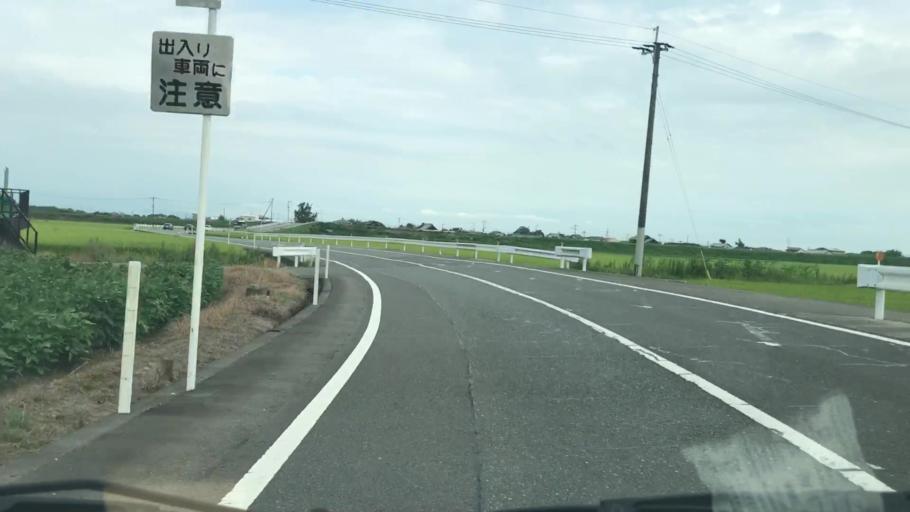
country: JP
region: Saga Prefecture
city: Saga-shi
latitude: 33.2886
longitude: 130.2413
